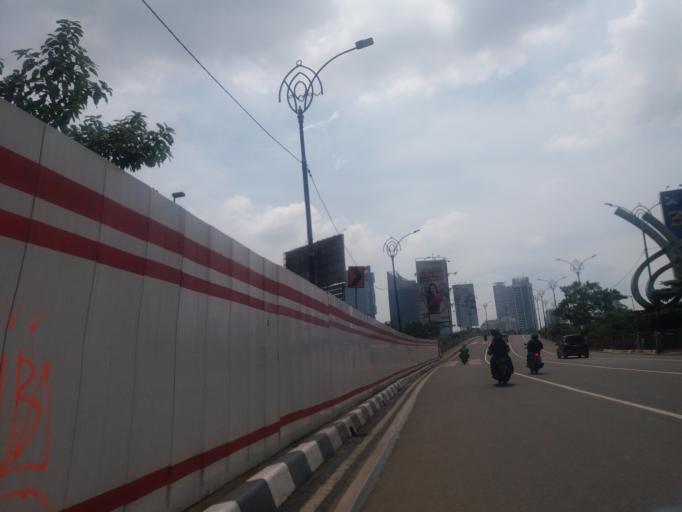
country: ID
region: Jakarta Raya
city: Jakarta
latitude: -6.2060
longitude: 106.8286
